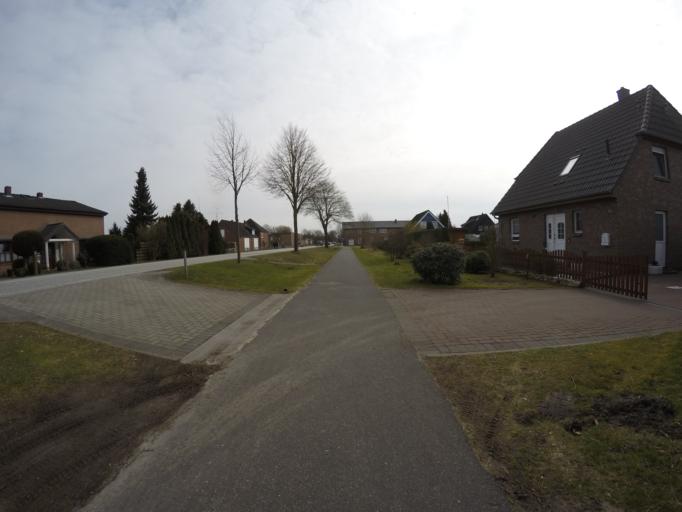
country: DE
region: Schleswig-Holstein
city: Bilsen
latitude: 53.7740
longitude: 9.8756
